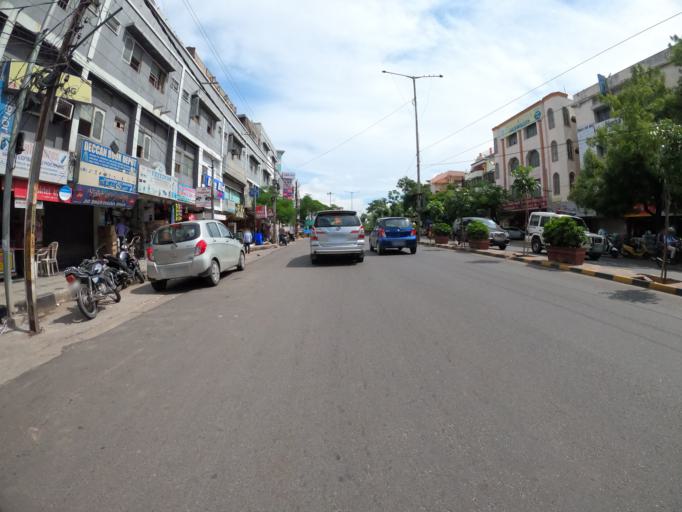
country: IN
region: Telangana
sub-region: Hyderabad
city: Hyderabad
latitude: 17.3943
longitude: 78.4271
